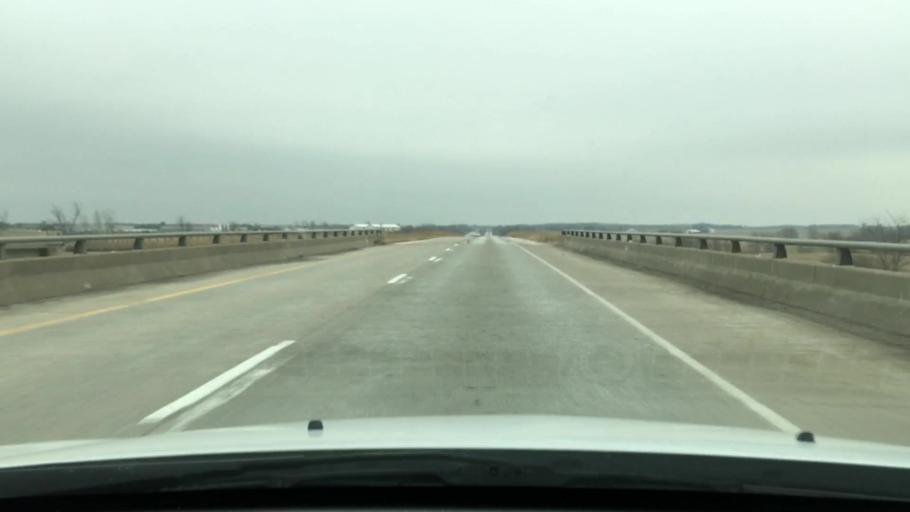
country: US
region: Illinois
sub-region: Morgan County
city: South Jacksonville
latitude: 39.7103
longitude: -90.1805
